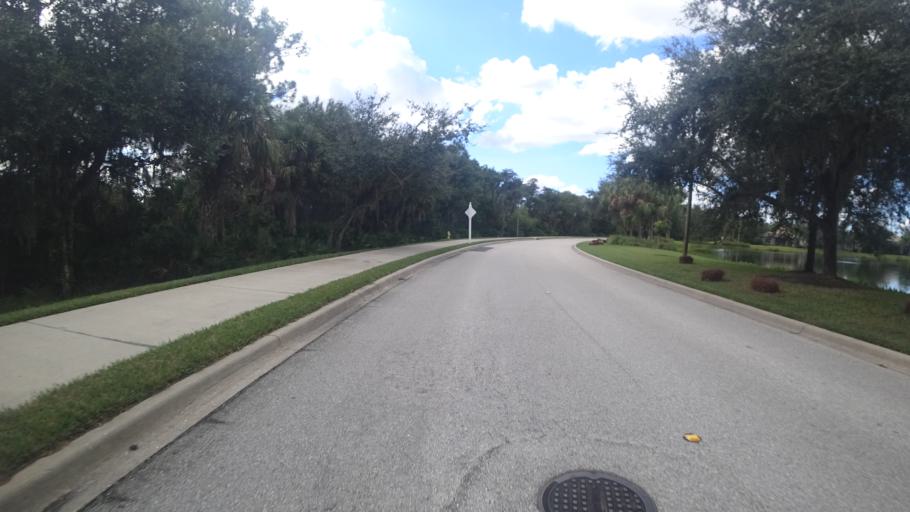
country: US
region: Florida
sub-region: Sarasota County
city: The Meadows
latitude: 27.4053
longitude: -82.4241
